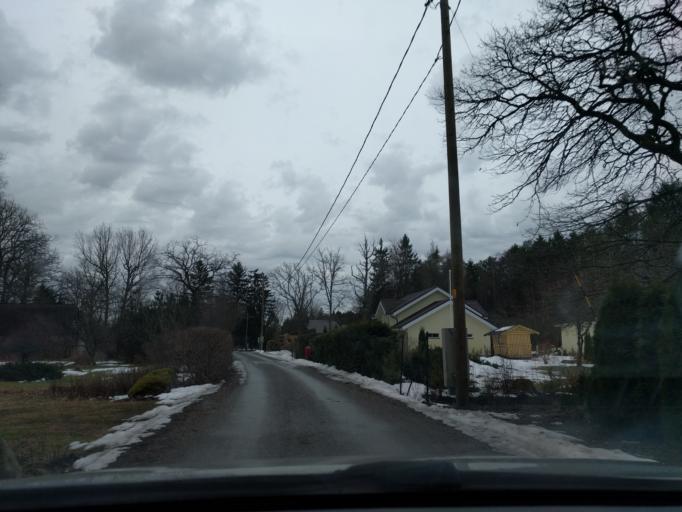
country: EE
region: Harju
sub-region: Viimsi vald
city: Viimsi
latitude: 59.5169
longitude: 24.9058
